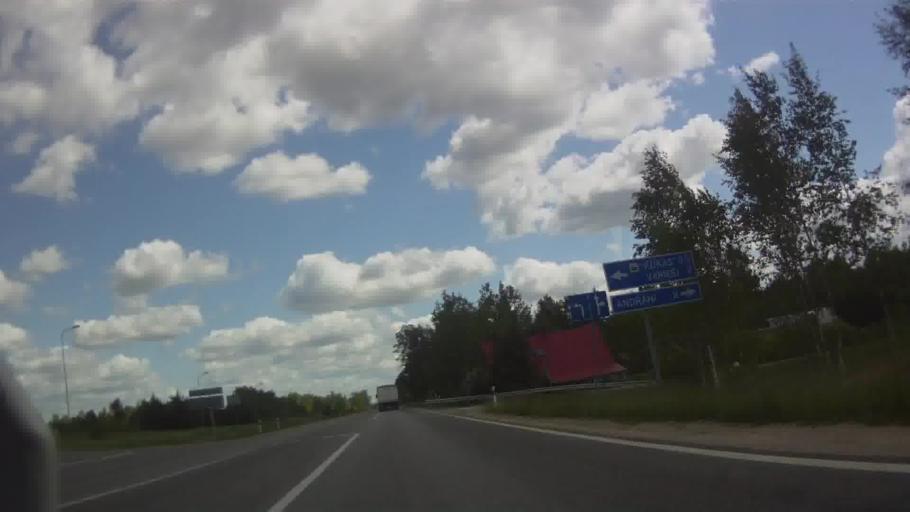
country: LV
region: Jekabpils Rajons
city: Jekabpils
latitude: 56.5400
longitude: 26.0667
